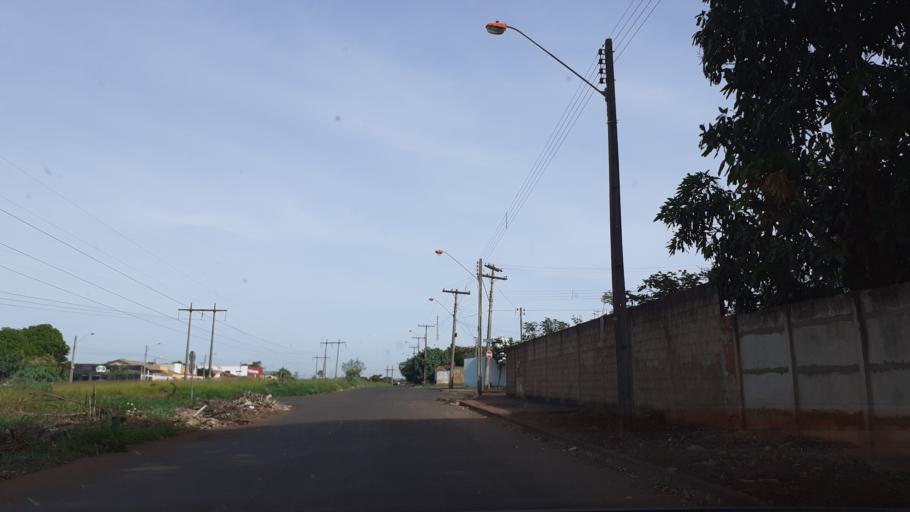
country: BR
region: Goias
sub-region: Itumbiara
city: Itumbiara
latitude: -18.4191
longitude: -49.2417
